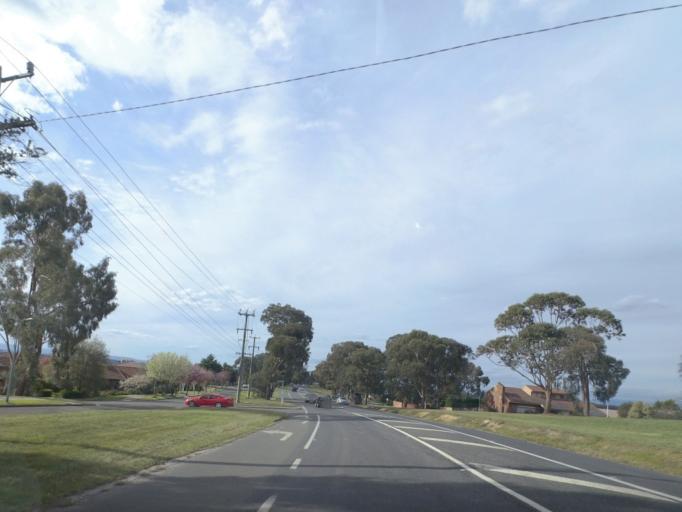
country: AU
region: Victoria
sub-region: Manningham
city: Donvale
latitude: -37.7753
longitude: 145.1677
